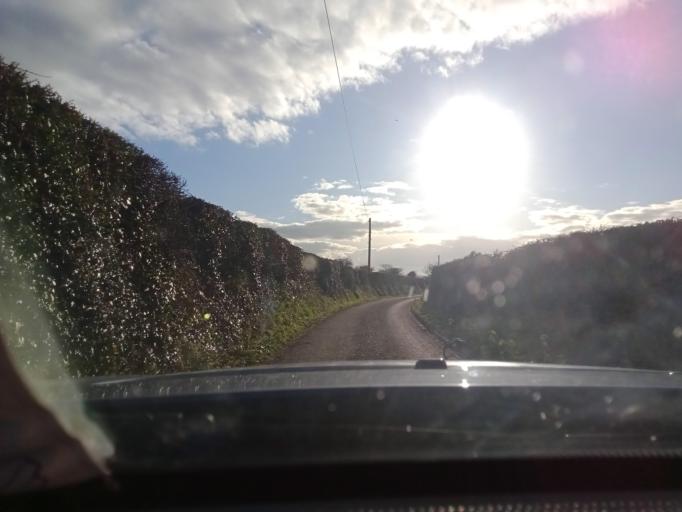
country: IE
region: Leinster
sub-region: Kilkenny
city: Graiguenamanagh
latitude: 52.5564
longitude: -6.9480
